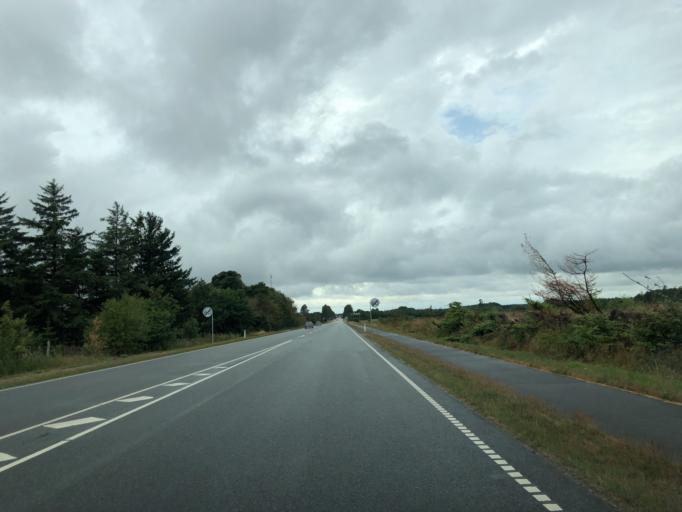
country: DK
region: Central Jutland
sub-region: Ikast-Brande Kommune
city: Ikast
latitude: 56.1366
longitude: 9.1179
